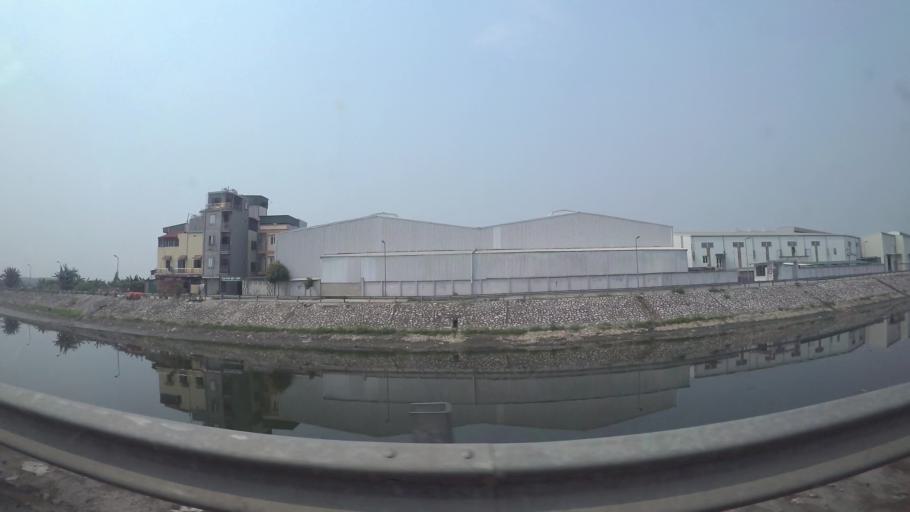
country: VN
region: Ha Noi
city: Van Dien
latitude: 20.9596
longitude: 105.8182
